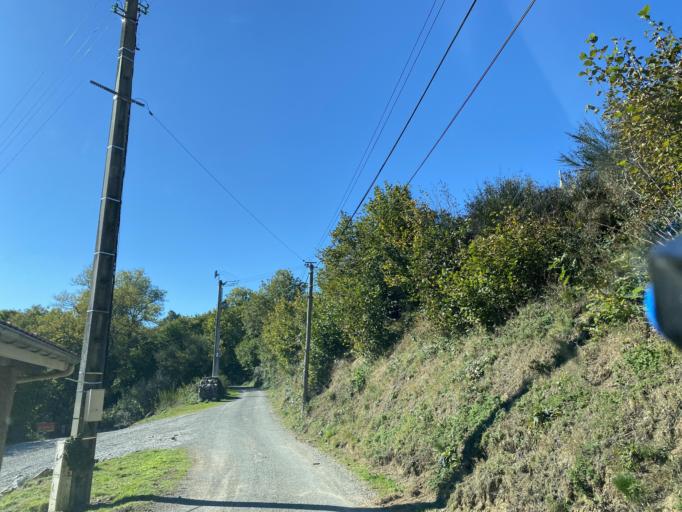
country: FR
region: Rhone-Alpes
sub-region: Departement de la Loire
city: Saint-Just-en-Chevalet
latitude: 45.9584
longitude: 3.8631
